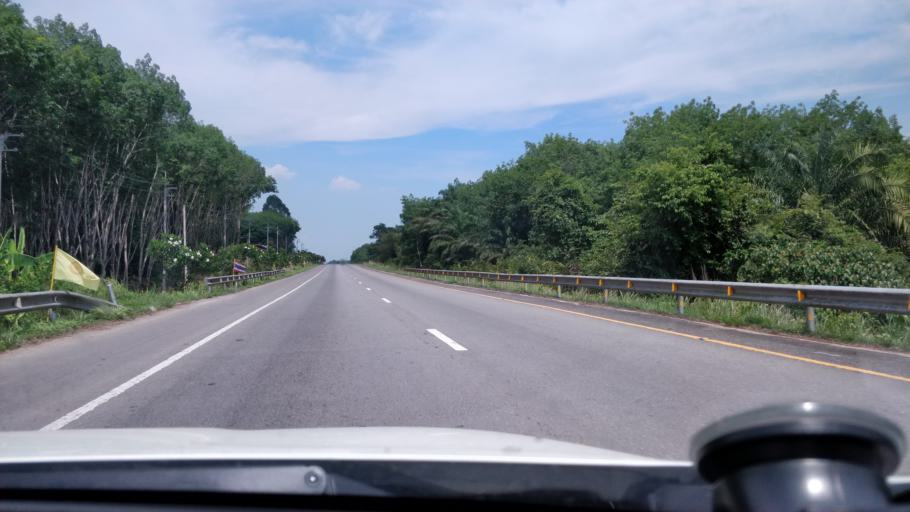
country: TH
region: Surat Thani
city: Chai Buri
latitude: 8.6415
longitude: 99.0708
